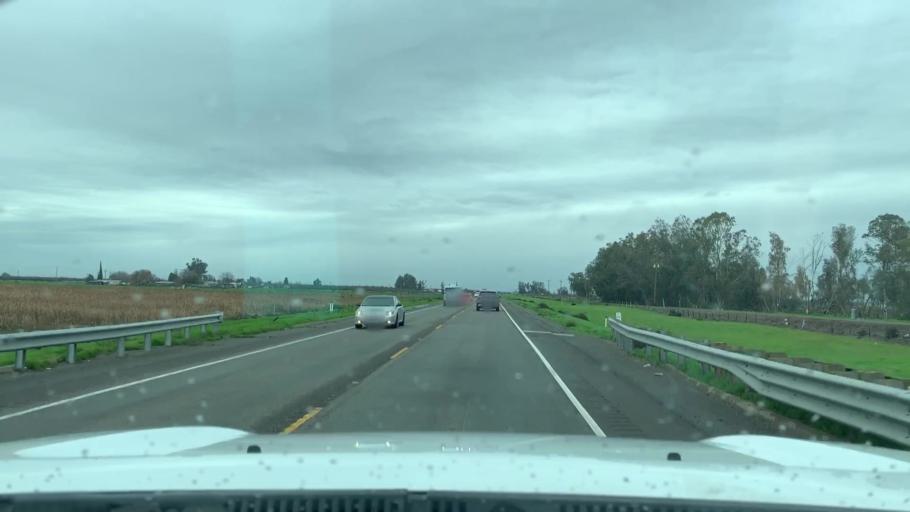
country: US
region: California
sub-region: Fresno County
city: Riverdale
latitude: 36.4590
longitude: -119.7960
